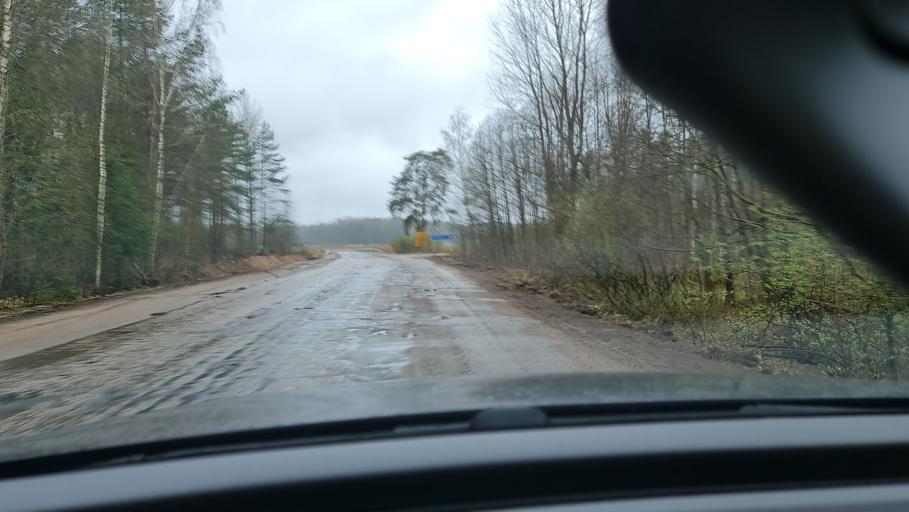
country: RU
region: Novgorod
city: Valday
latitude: 58.0406
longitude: 32.9098
